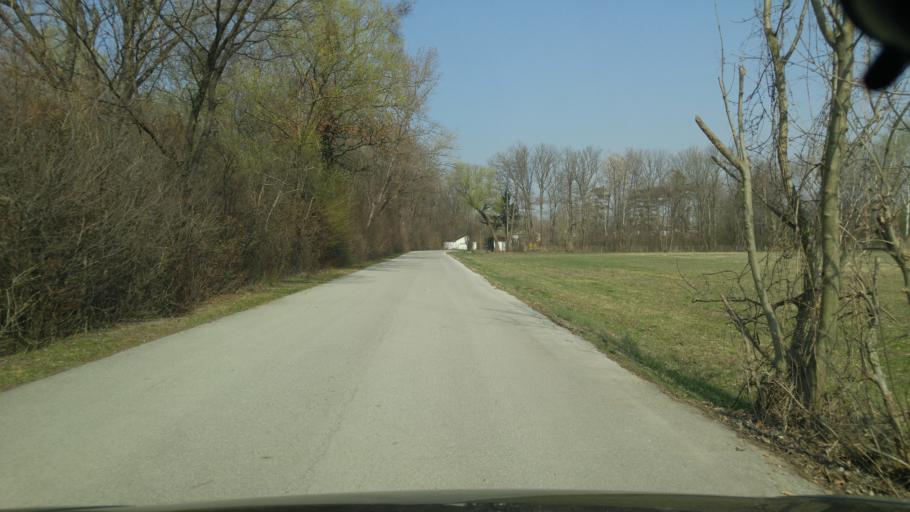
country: AT
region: Lower Austria
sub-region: Politischer Bezirk Wien-Umgebung
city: Moosbrunn
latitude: 48.0379
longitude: 16.4341
